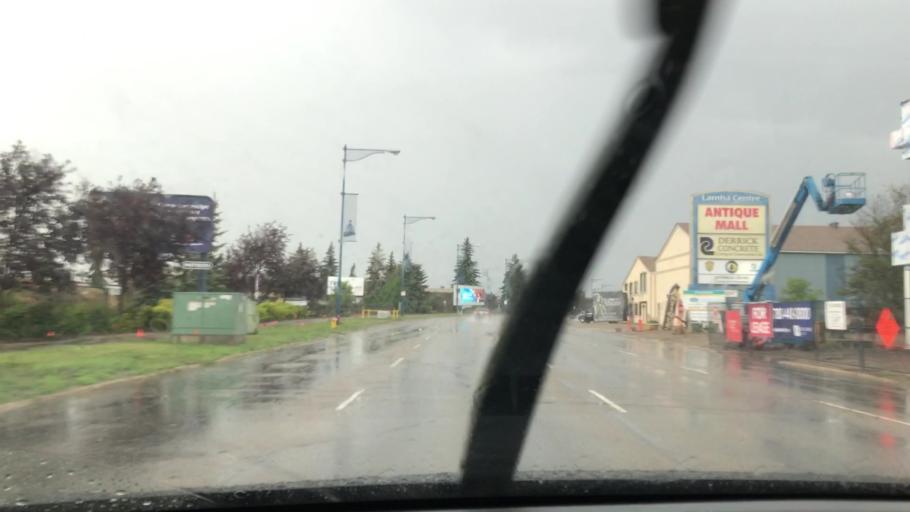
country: CA
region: Alberta
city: Edmonton
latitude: 53.5060
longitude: -113.4948
